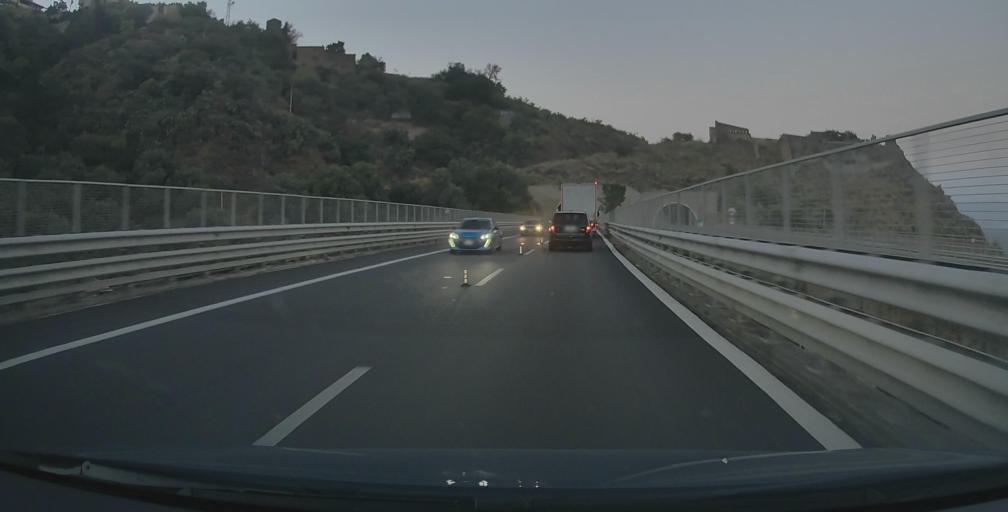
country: IT
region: Sicily
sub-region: Messina
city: Scaletta Zanclea
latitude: 38.0498
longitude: 15.4672
